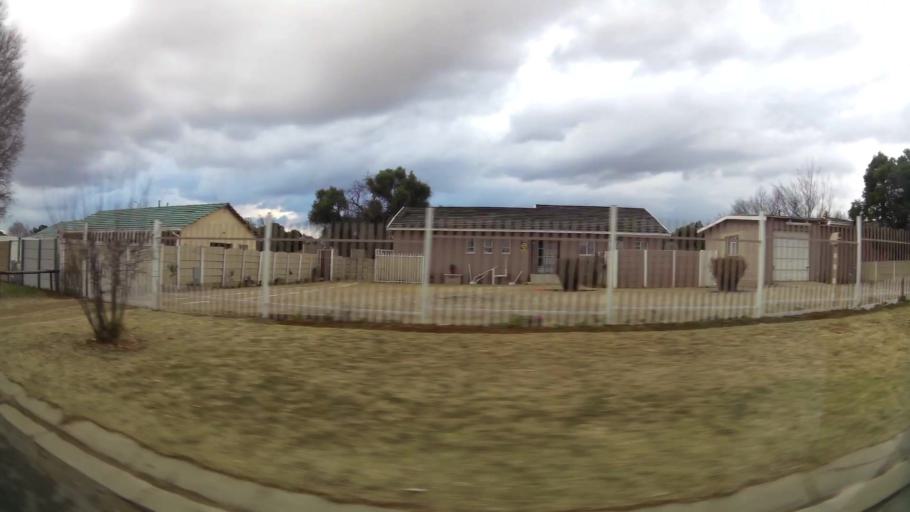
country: ZA
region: Orange Free State
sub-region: Lejweleputswa District Municipality
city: Welkom
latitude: -27.9630
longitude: 26.7204
